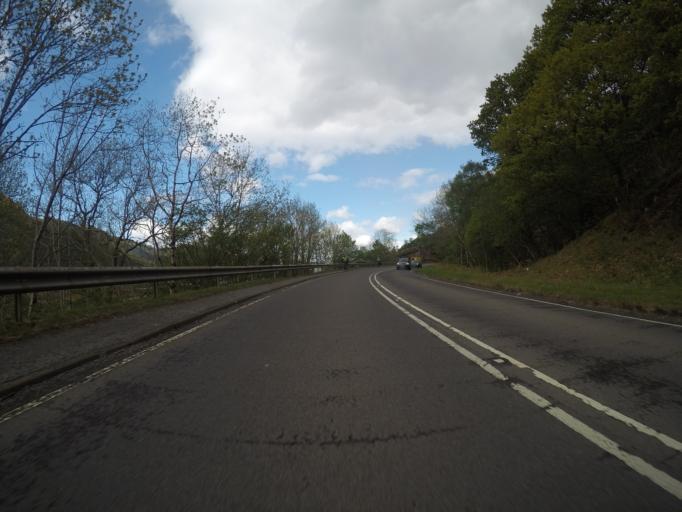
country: GB
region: Scotland
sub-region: Highland
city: Fort William
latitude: 57.2148
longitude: -5.4229
